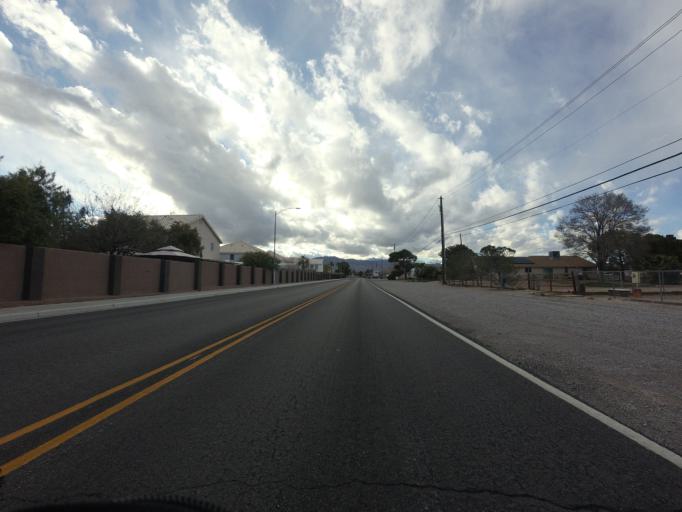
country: US
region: Nevada
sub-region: Clark County
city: Las Vegas
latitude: 36.2699
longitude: -115.2491
